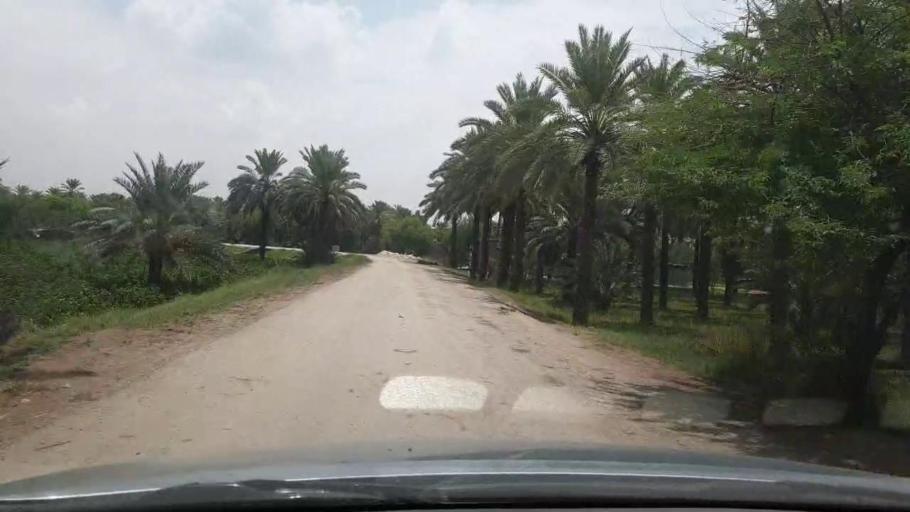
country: PK
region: Sindh
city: Khairpur
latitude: 27.4340
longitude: 68.7672
